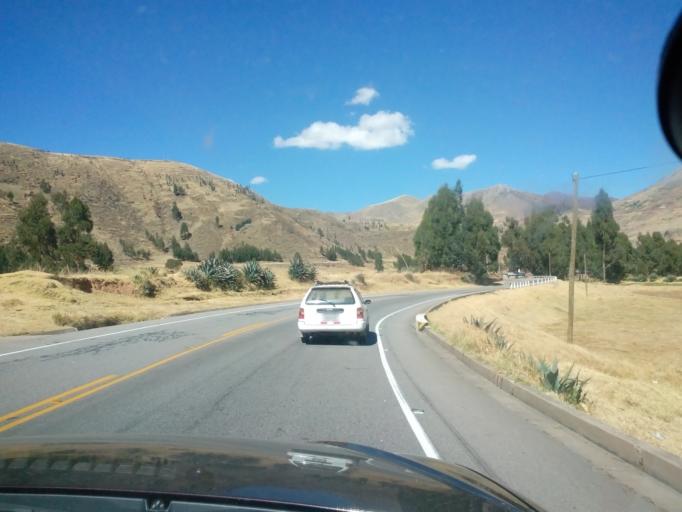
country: PE
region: Cusco
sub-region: Provincia de Canchis
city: Combapata
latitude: -14.0809
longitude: -71.4375
